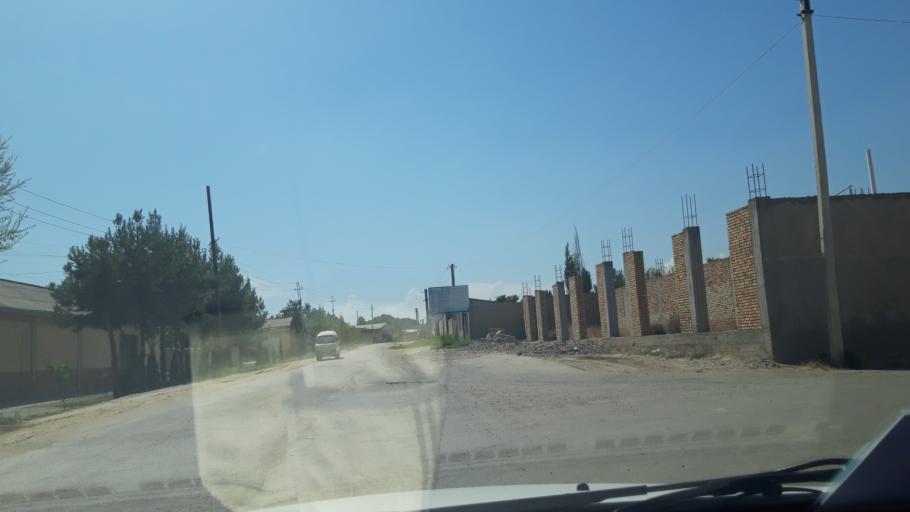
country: UZ
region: Namangan
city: Namangan
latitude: 41.0400
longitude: 71.6954
